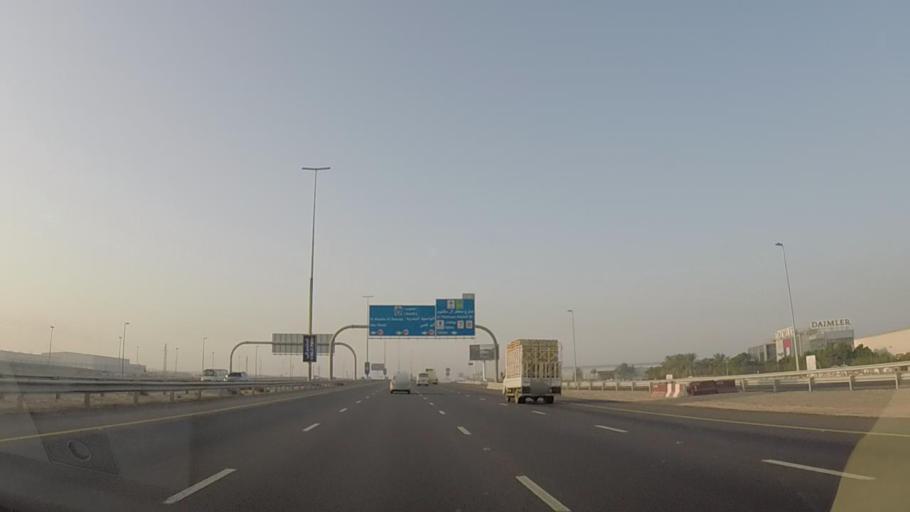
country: AE
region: Dubai
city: Dubai
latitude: 24.9618
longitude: 55.0815
